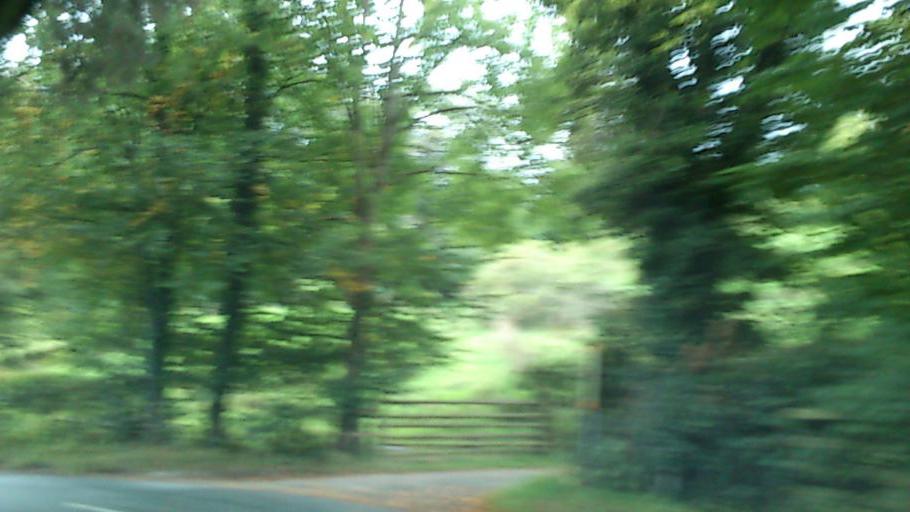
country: GB
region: Wales
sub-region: Sir Powys
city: Llanfyllin
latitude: 52.6452
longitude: -3.2814
